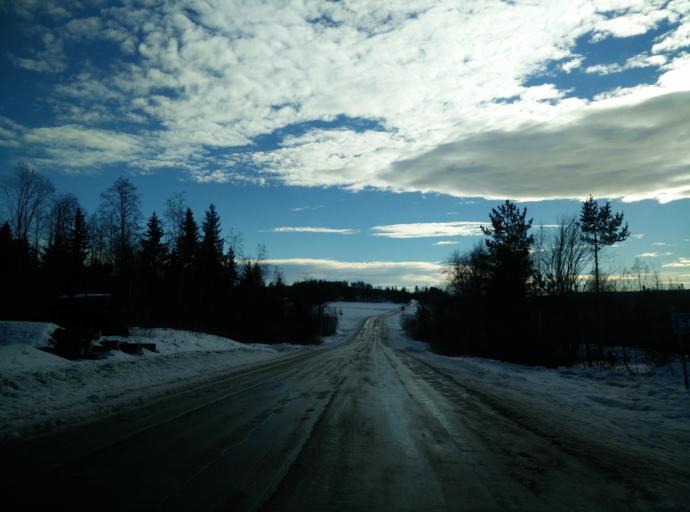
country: SE
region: Vaesternorrland
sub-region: Sundsvalls Kommun
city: Njurundabommen
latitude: 62.2604
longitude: 17.3842
